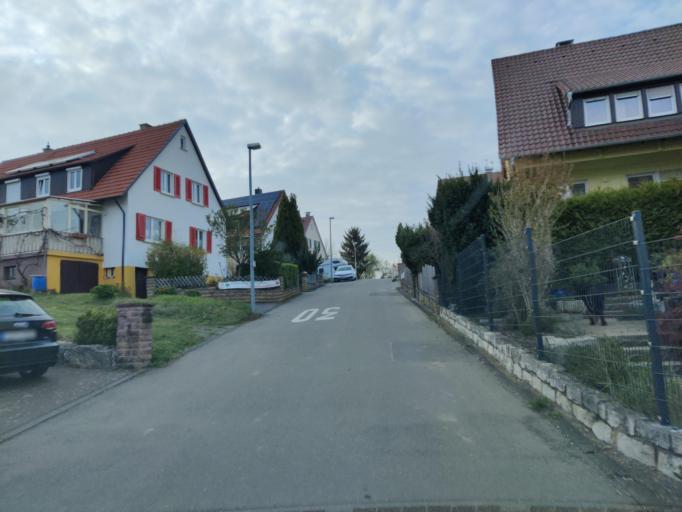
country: DE
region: Baden-Wuerttemberg
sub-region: Tuebingen Region
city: Dusslingen
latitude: 48.4503
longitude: 9.0510
